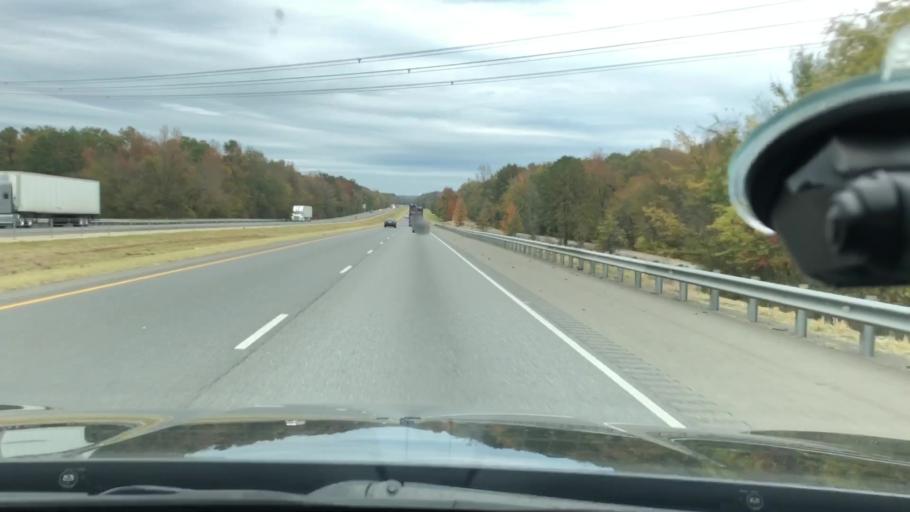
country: US
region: Arkansas
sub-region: Hot Spring County
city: Malvern
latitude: 34.3581
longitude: -92.8799
